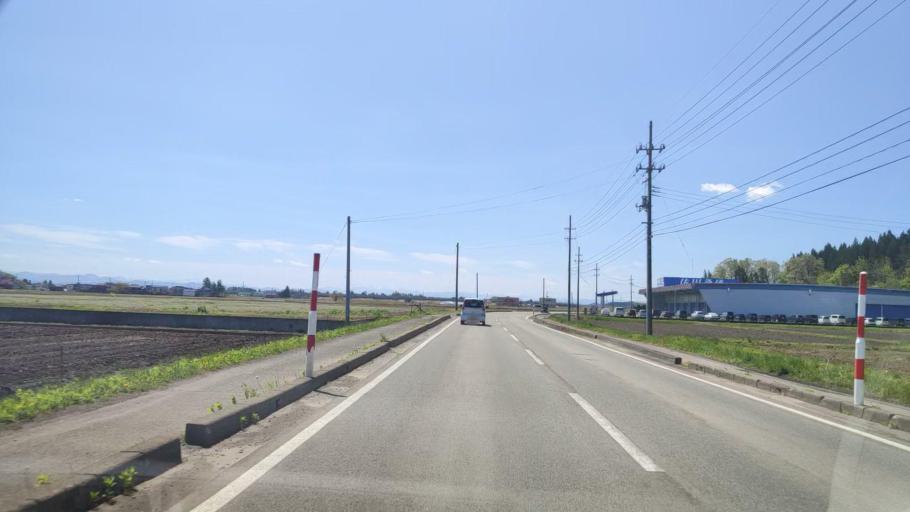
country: JP
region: Akita
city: Omagari
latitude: 39.4421
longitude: 140.4485
